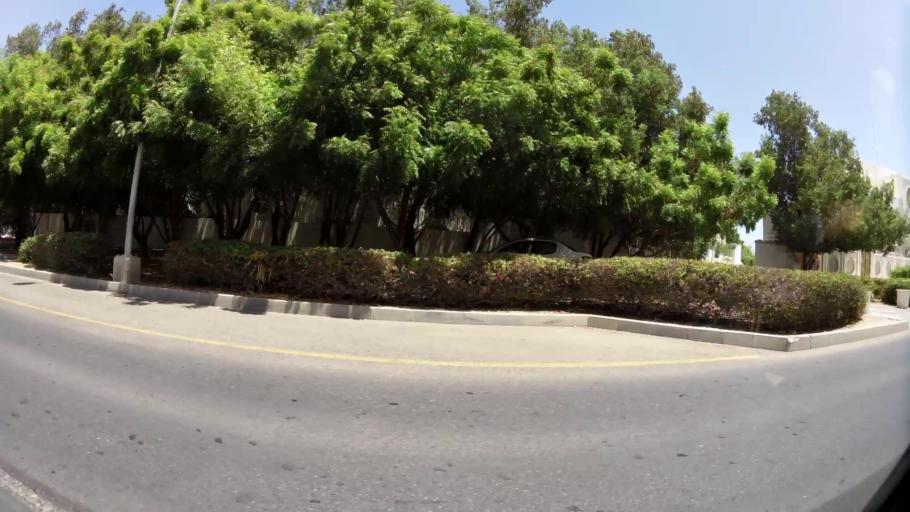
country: OM
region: Muhafazat Masqat
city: Bawshar
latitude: 23.6084
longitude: 58.4495
